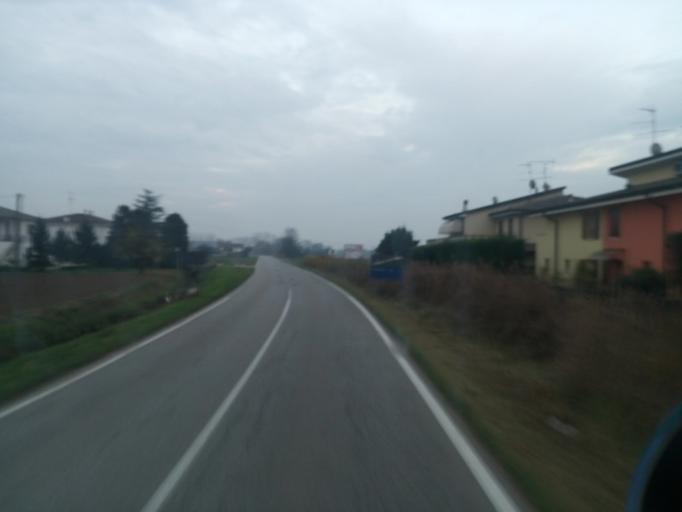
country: IT
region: Lombardy
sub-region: Provincia di Mantova
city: Gazzo
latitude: 45.1595
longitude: 10.8959
